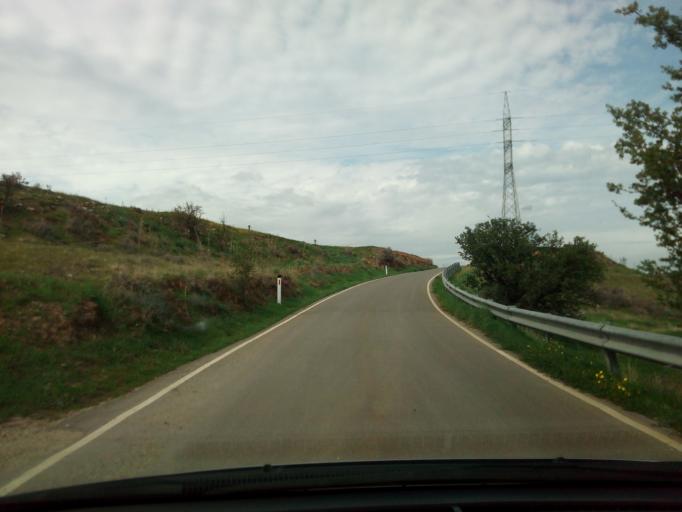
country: CY
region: Lefkosia
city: Astromeritis
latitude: 35.0958
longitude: 32.9880
